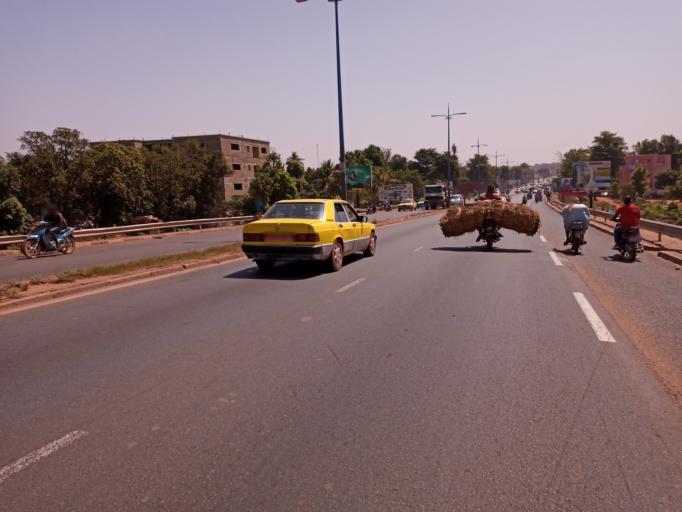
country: ML
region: Bamako
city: Bamako
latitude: 12.6197
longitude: -8.0020
